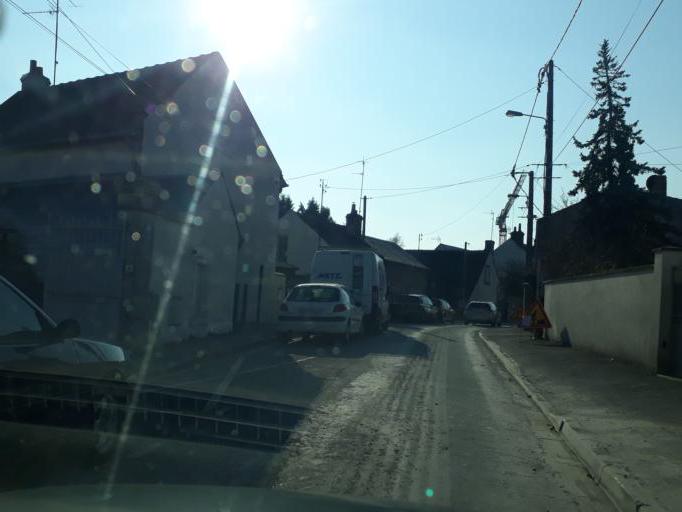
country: FR
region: Centre
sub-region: Departement du Loiret
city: Saint-Jean-le-Blanc
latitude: 47.9053
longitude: 1.9384
